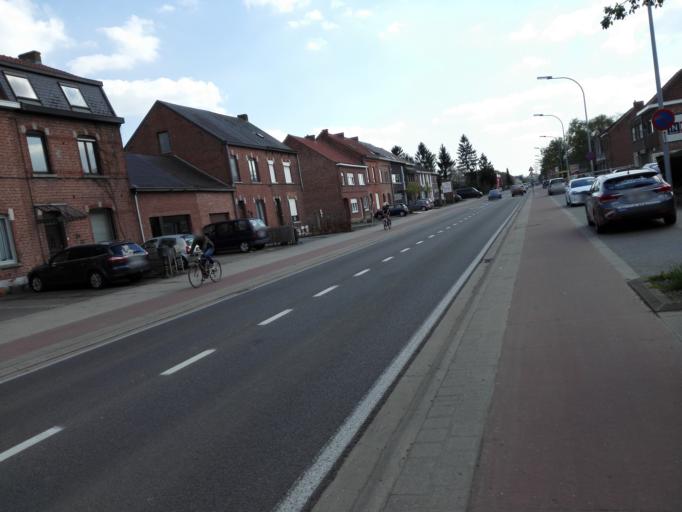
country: BE
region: Flanders
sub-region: Provincie Vlaams-Brabant
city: Rotselaar
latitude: 50.9157
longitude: 4.7164
